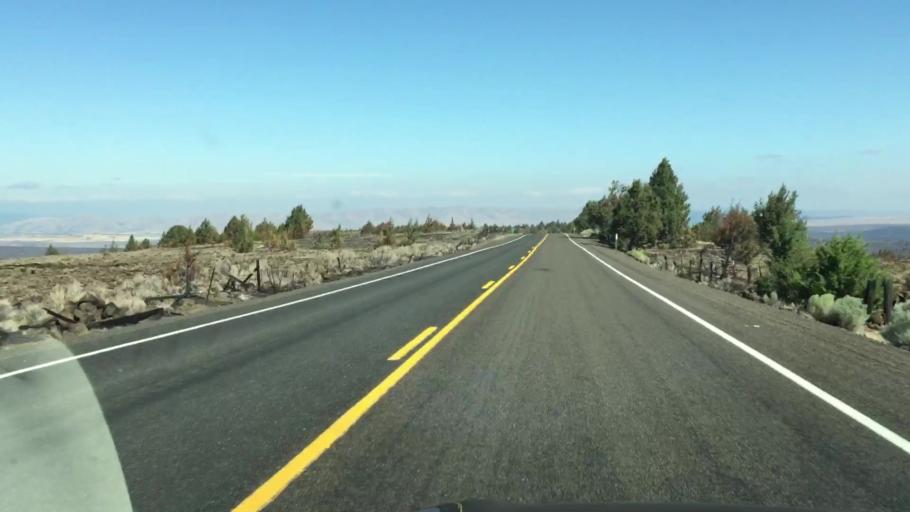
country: US
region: Oregon
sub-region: Jefferson County
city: Warm Springs
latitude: 45.0737
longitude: -121.0233
